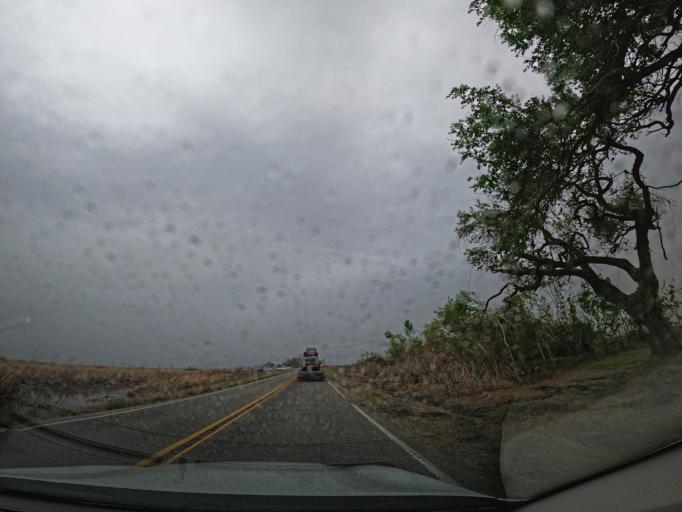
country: US
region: Louisiana
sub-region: Cameron Parish
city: Cameron
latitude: 29.7759
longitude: -93.0435
